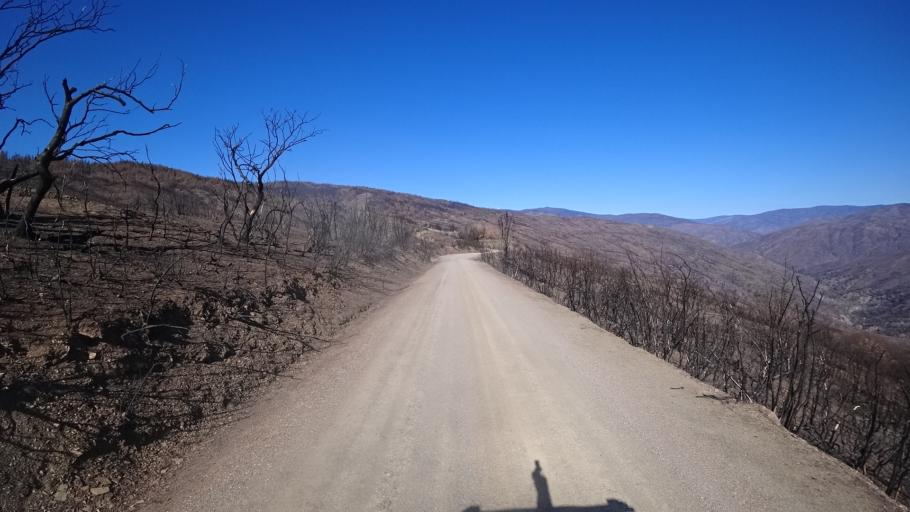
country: US
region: California
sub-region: Tehama County
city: Rancho Tehama Reserve
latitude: 39.6665
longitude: -122.6652
